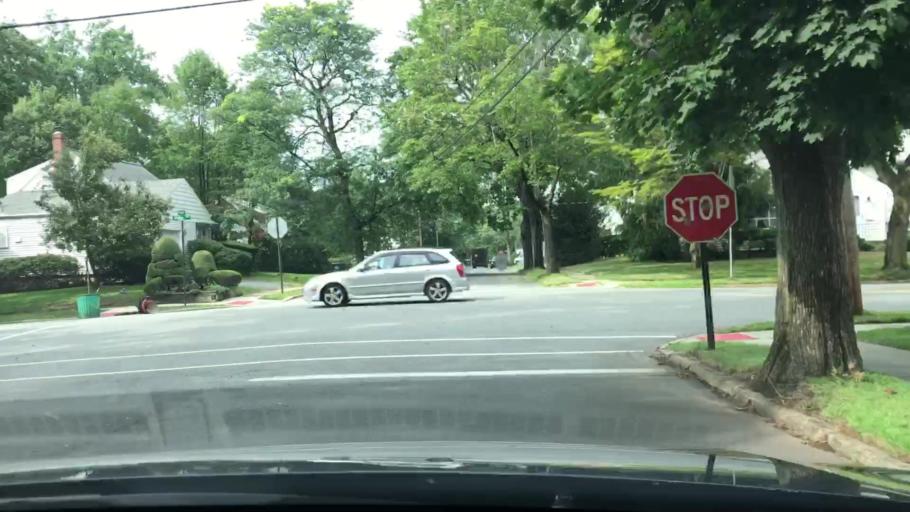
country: US
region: New Jersey
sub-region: Bergen County
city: Bergenfield
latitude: 40.9291
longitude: -74.0086
